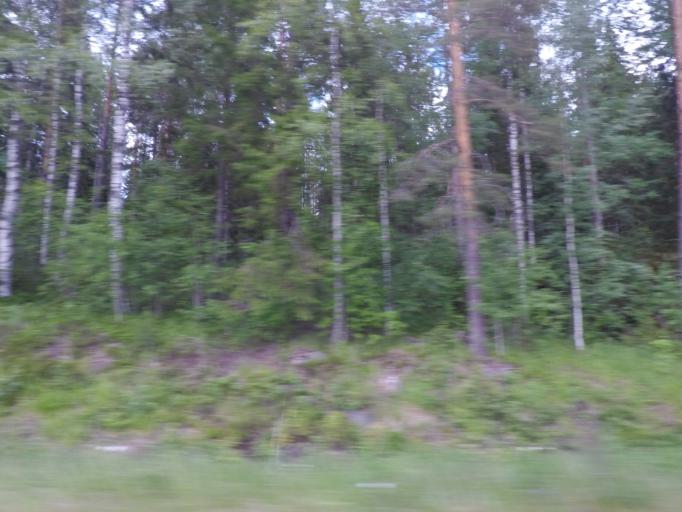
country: FI
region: Paijanne Tavastia
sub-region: Lahti
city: Hollola
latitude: 60.8434
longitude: 25.4946
